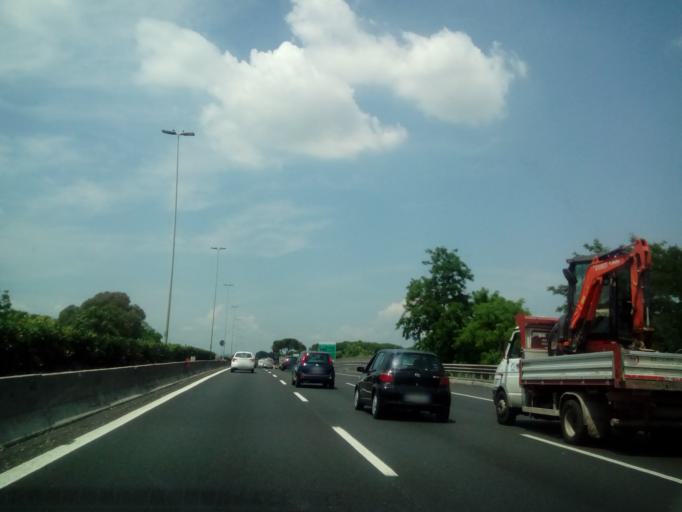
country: IT
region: Latium
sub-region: Citta metropolitana di Roma Capitale
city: Setteville
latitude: 41.9105
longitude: 12.6158
